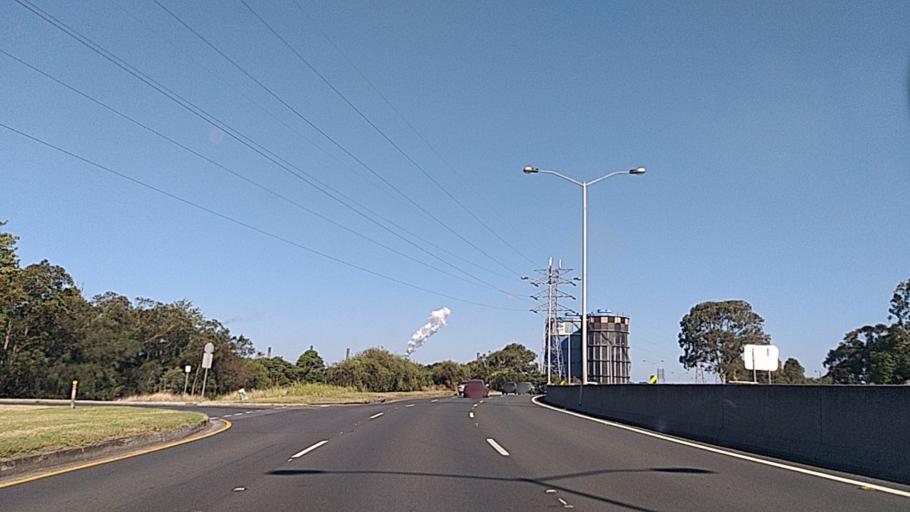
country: AU
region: New South Wales
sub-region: Wollongong
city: Cringila
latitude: -34.4659
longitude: 150.8762
